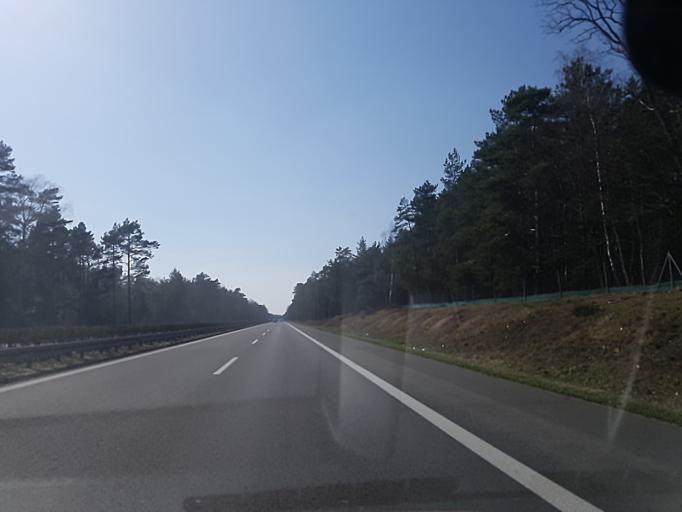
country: DE
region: Brandenburg
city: Forst
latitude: 51.7122
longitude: 14.5853
